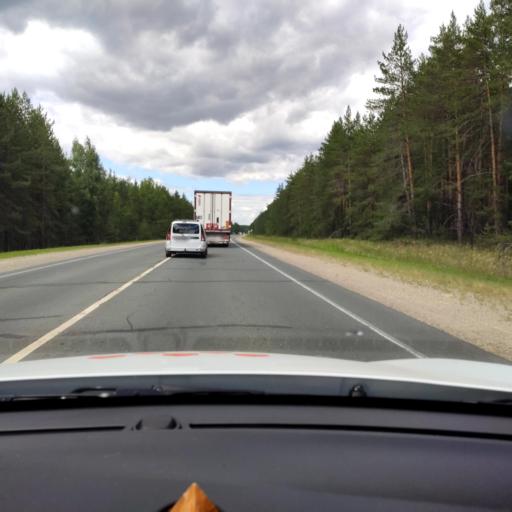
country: RU
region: Mariy-El
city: Krasnogorskiy
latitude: 56.1029
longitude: 48.3438
